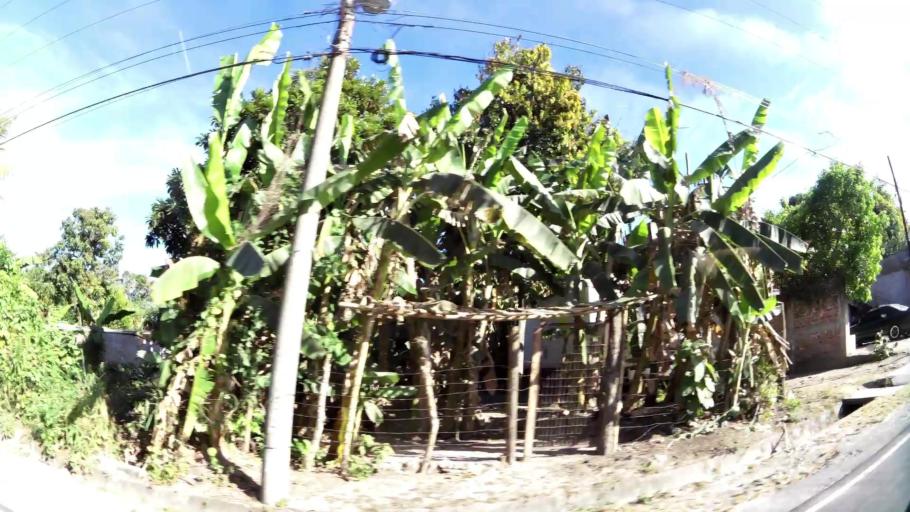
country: SV
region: Cuscatlan
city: Tecoluca
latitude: 13.7671
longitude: -89.0460
